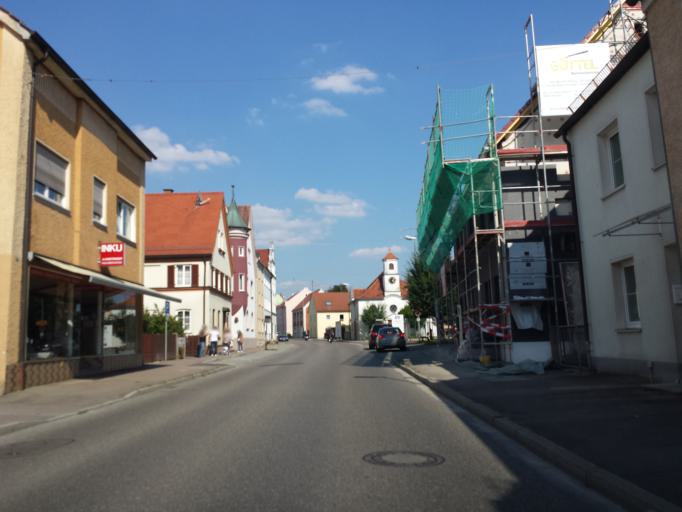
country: DE
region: Bavaria
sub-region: Swabia
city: Ichenhausen
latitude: 48.3726
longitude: 10.3076
